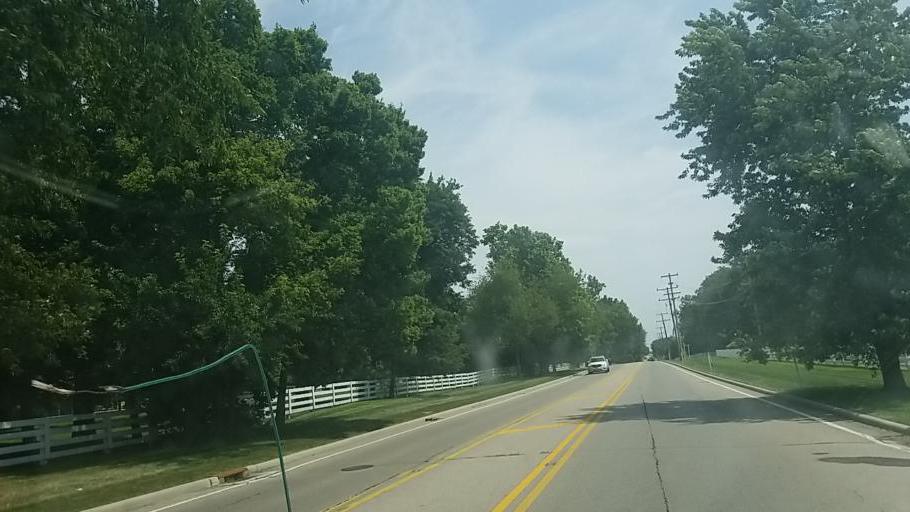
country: US
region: Ohio
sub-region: Franklin County
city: New Albany
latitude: 40.0542
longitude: -82.8377
